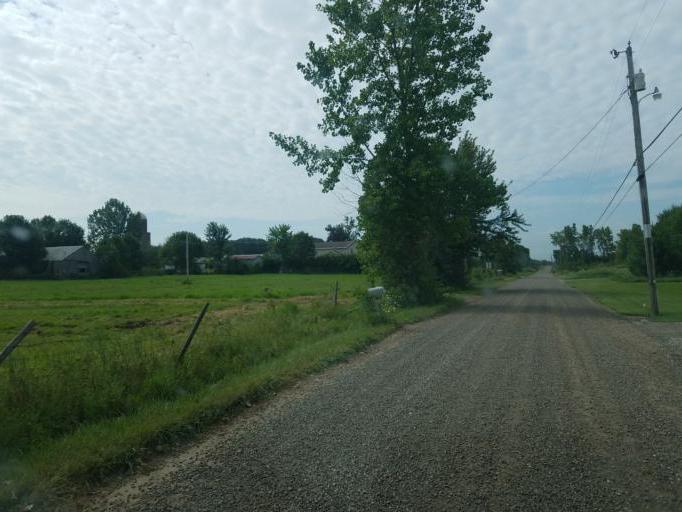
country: US
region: Ohio
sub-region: Morrow County
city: Mount Gilead
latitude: 40.4549
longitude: -82.7666
